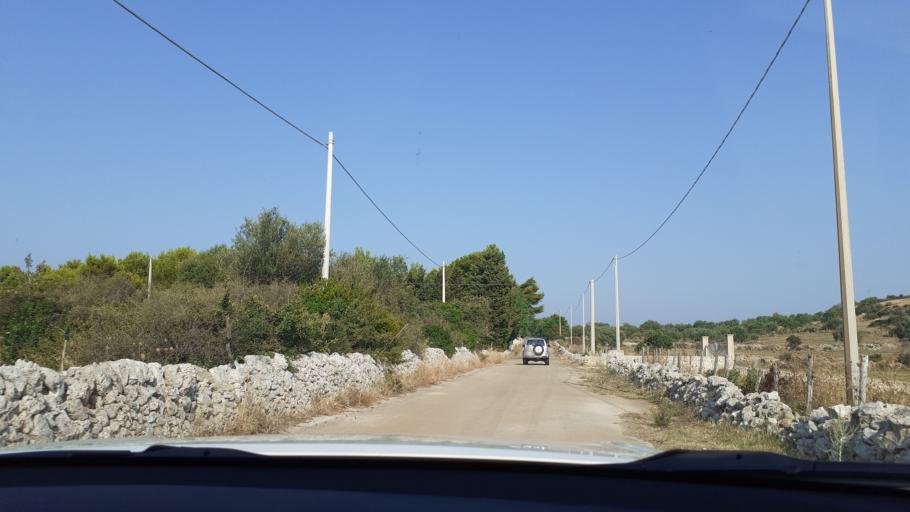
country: IT
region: Sicily
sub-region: Provincia di Siracusa
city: Cassibile
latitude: 36.9776
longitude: 15.1525
